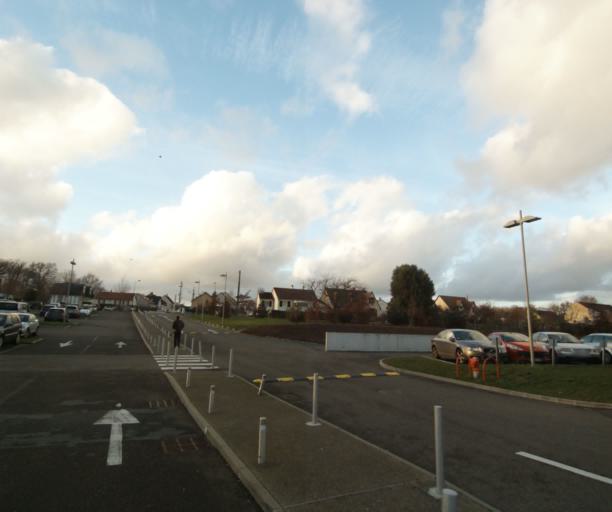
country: FR
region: Pays de la Loire
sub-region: Departement de la Sarthe
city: Le Mans
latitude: 47.9653
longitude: 0.2245
